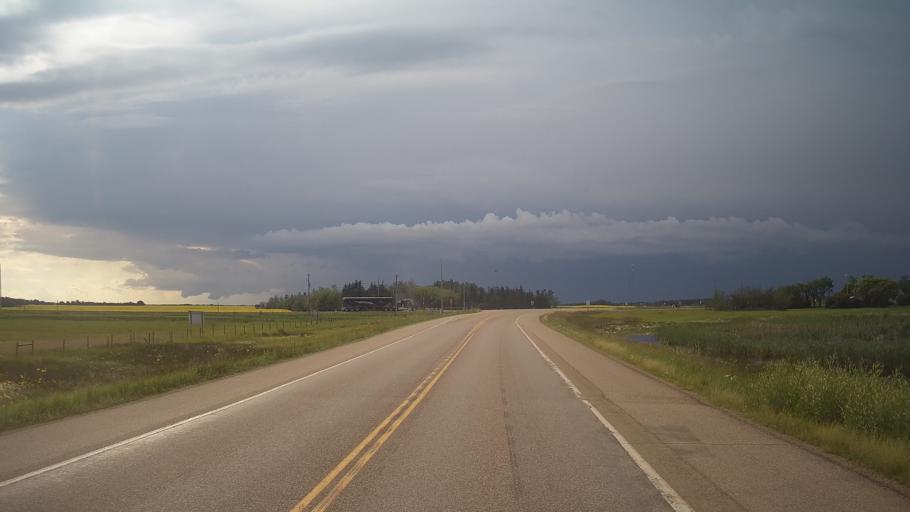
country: CA
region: Alberta
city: Vegreville
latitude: 53.2297
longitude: -112.2427
